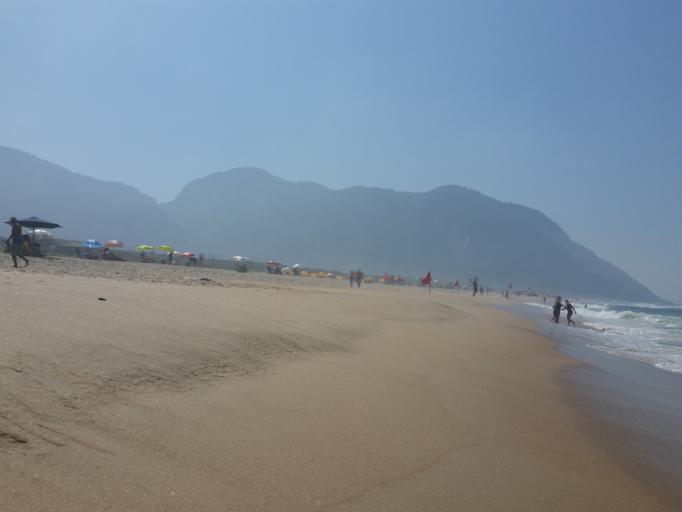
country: BR
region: Rio de Janeiro
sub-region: Nilopolis
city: Nilopolis
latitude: -23.0505
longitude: -43.5342
